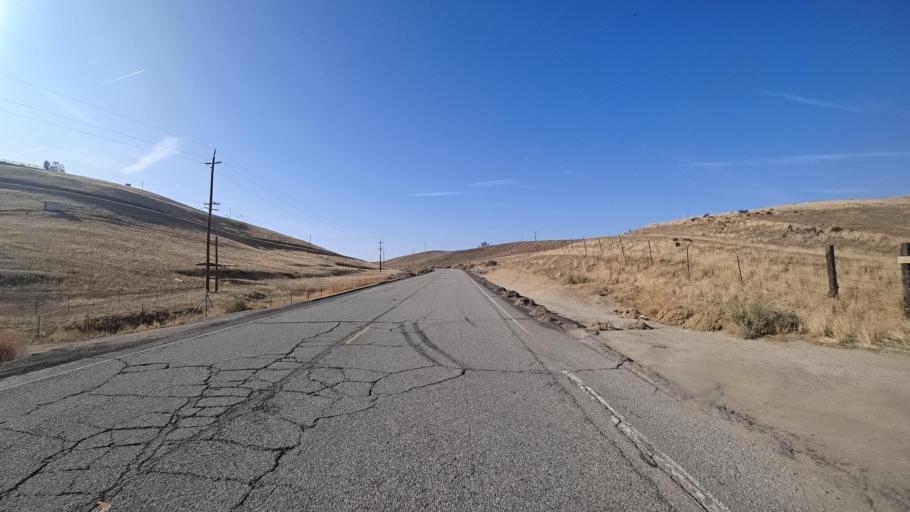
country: US
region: California
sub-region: Kern County
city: Oildale
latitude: 35.5010
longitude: -118.9922
